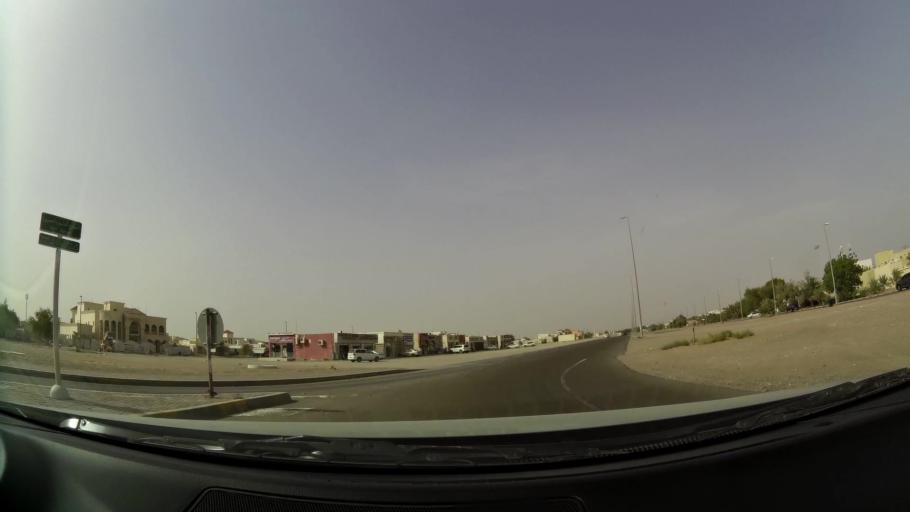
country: AE
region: Abu Dhabi
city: Al Ain
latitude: 24.2082
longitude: 55.5891
